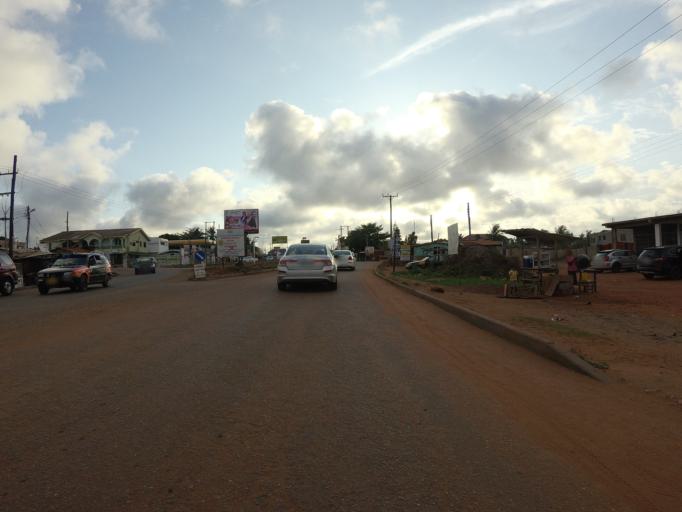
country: GH
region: Greater Accra
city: Teshi Old Town
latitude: 5.6100
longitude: -0.1070
